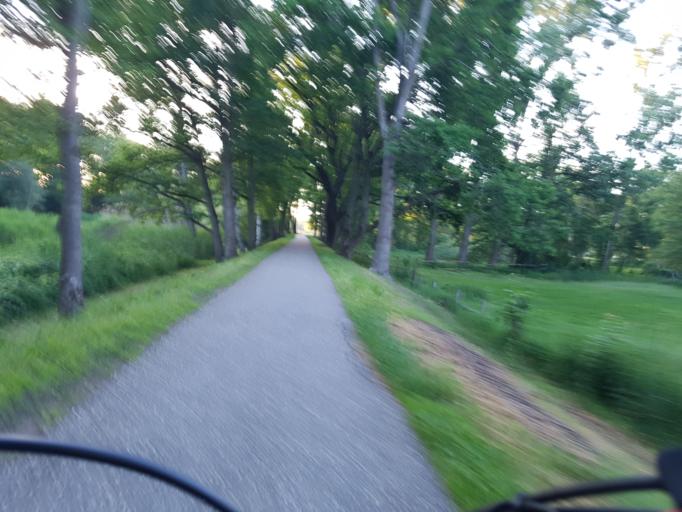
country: DE
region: Brandenburg
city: Schilda
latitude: 51.5725
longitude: 13.3486
